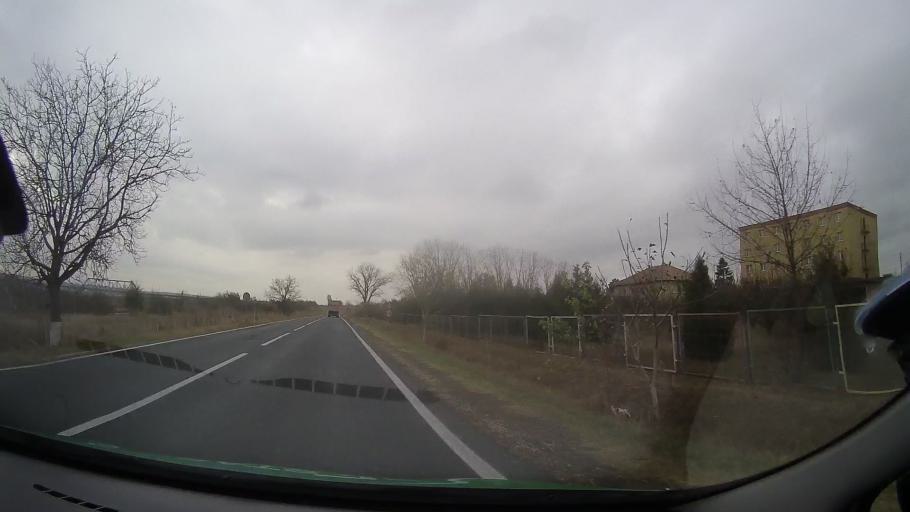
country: RO
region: Constanta
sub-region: Comuna Castelu
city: Castelu
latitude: 44.2531
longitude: 28.3240
